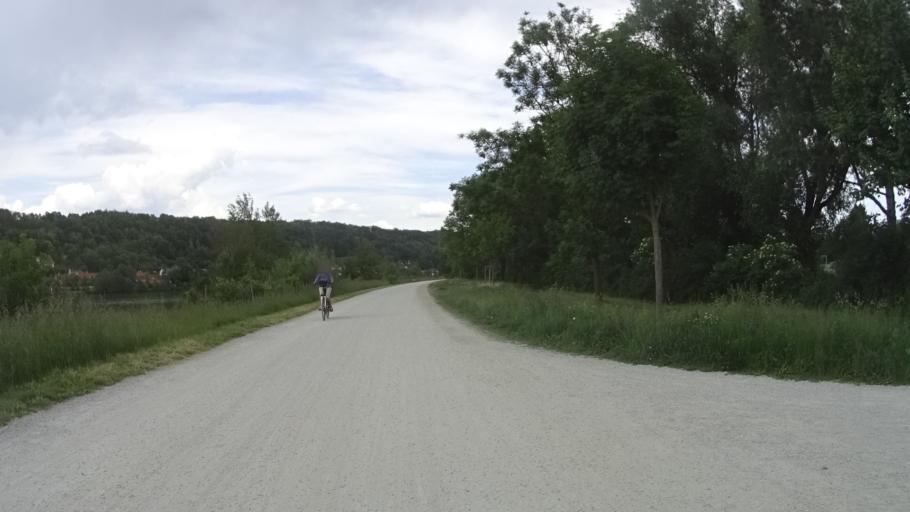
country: DE
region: Bavaria
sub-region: Upper Palatinate
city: Lappersdorf
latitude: 49.0297
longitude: 12.0594
